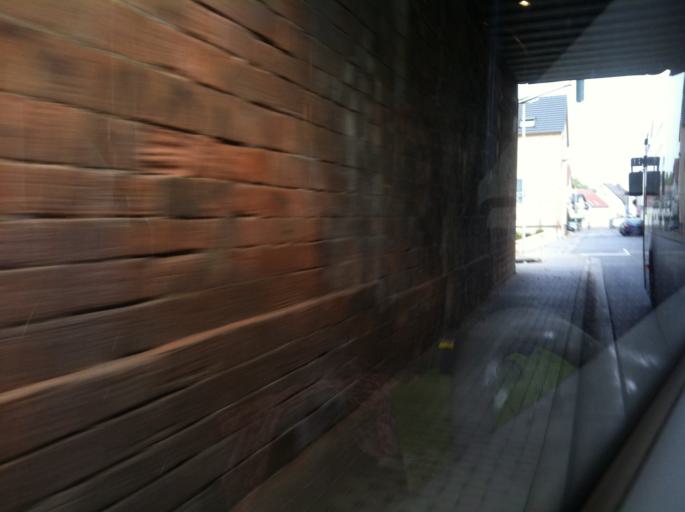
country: DE
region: Rheinland-Pfalz
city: Klein-Winternheim
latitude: 49.9599
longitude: 8.2165
